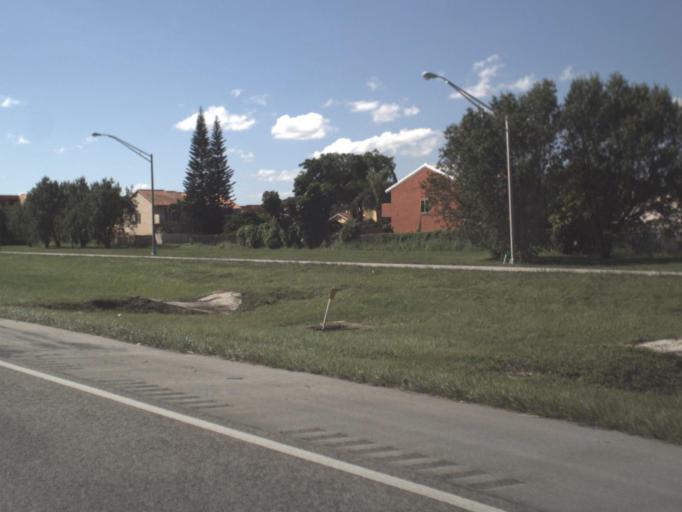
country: US
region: Florida
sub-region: Miami-Dade County
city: Tamiami
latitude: 25.7556
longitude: -80.3853
